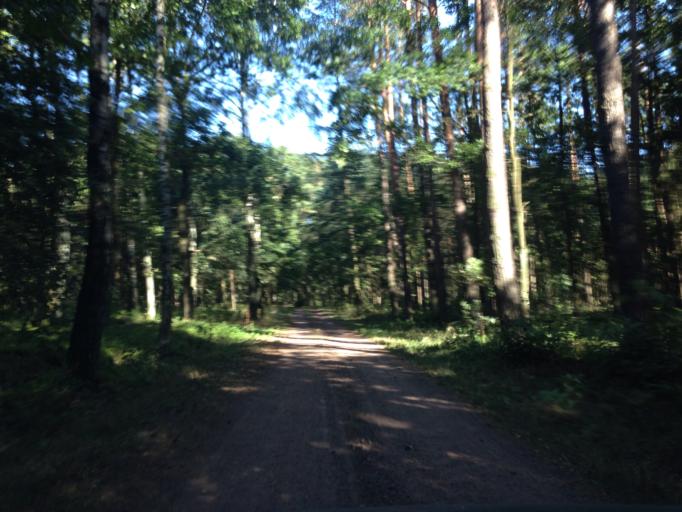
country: PL
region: Kujawsko-Pomorskie
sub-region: Powiat brodnicki
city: Gorzno
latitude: 53.1602
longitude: 19.6206
